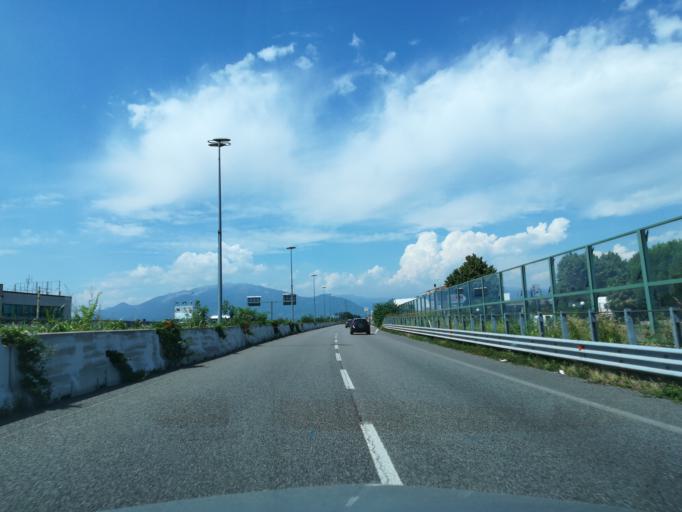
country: IT
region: Lombardy
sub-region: Provincia di Bergamo
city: Treviolo
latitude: 45.6696
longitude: 9.6016
